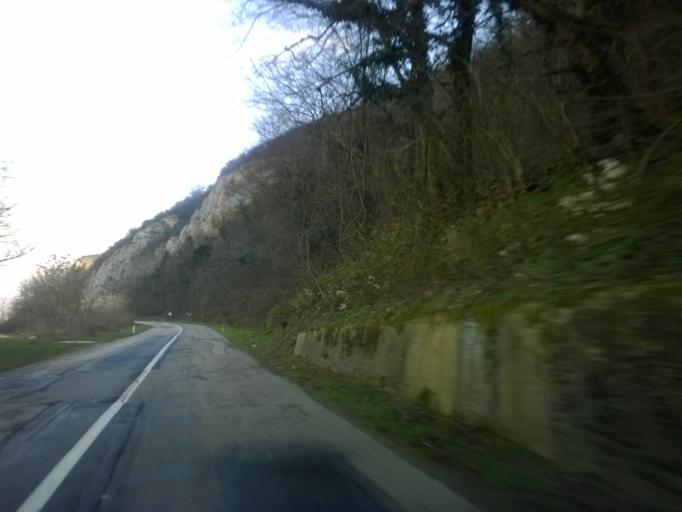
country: RO
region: Caras-Severin
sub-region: Comuna Pescari
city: Coronini
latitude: 44.6515
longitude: 21.7230
